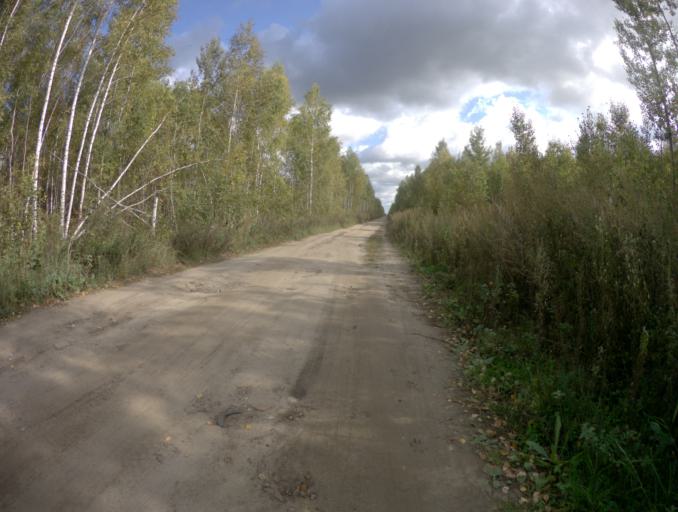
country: RU
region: Moskovskaya
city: Baksheyevo
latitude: 55.7163
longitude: 39.9216
